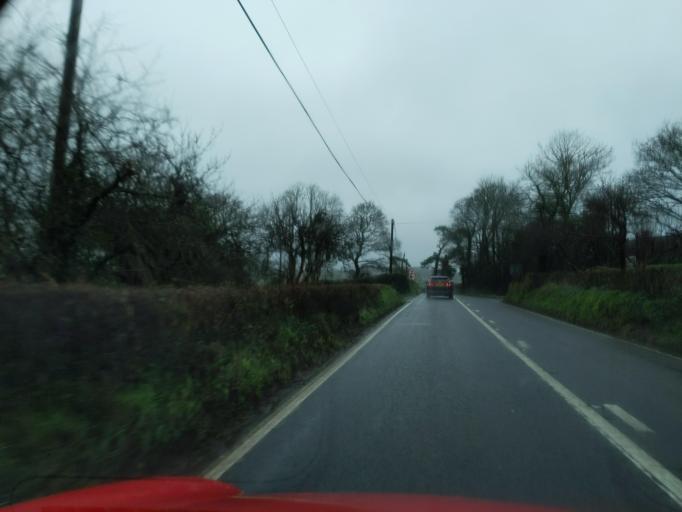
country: GB
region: England
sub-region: Cornwall
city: Launceston
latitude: 50.6081
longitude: -4.3375
